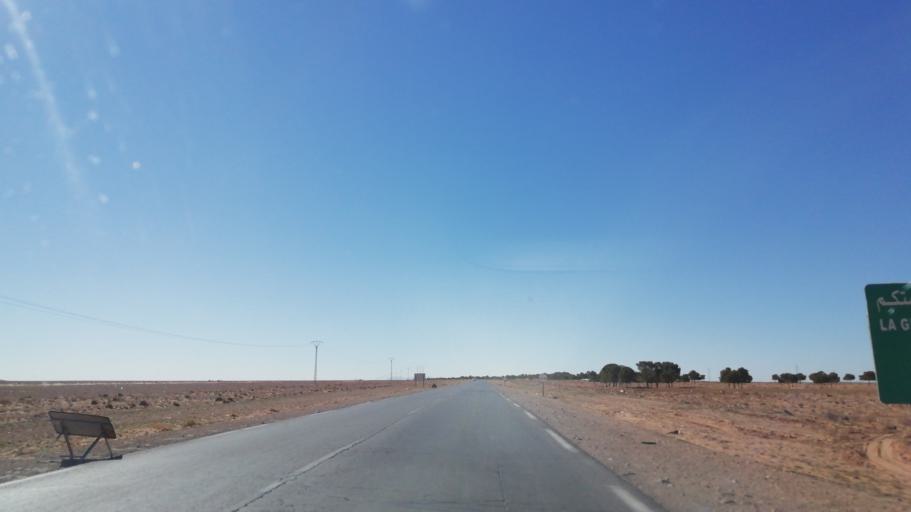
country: DZ
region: Saida
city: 'Ain el Hadjar
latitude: 34.0051
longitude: 0.0476
